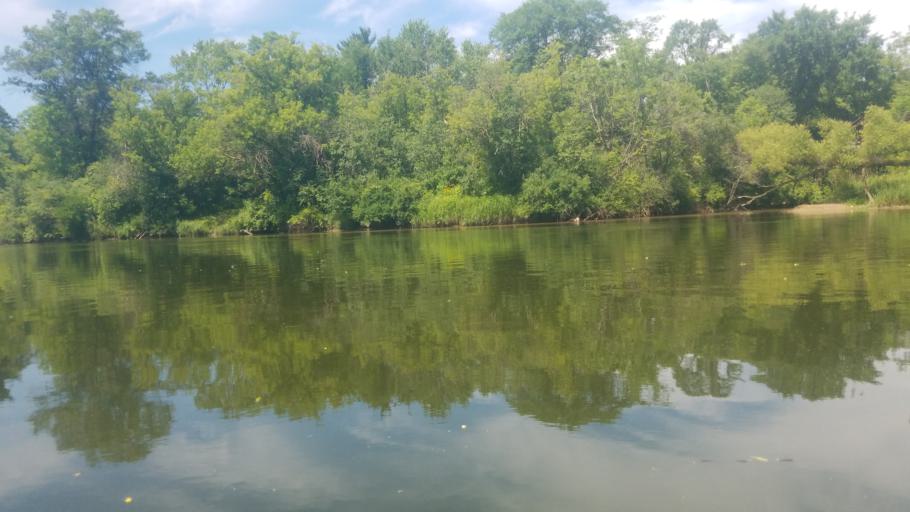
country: US
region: Wisconsin
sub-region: Dunn County
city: Menomonie
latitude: 44.8720
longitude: -91.9411
